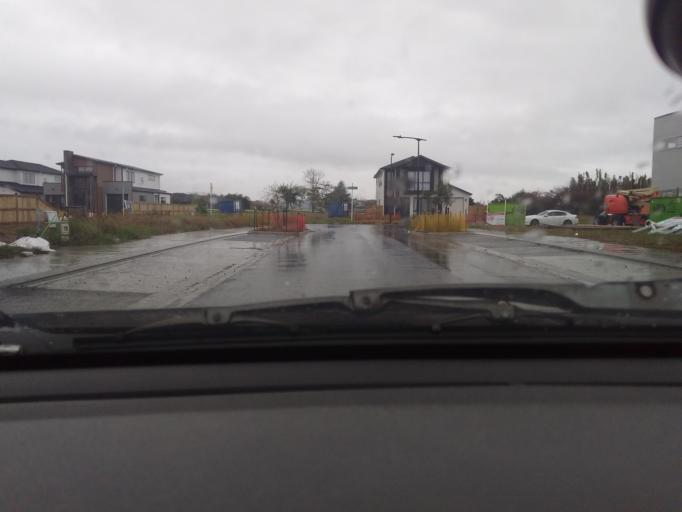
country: NZ
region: Auckland
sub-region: Auckland
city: Rosebank
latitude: -36.8044
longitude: 174.6635
